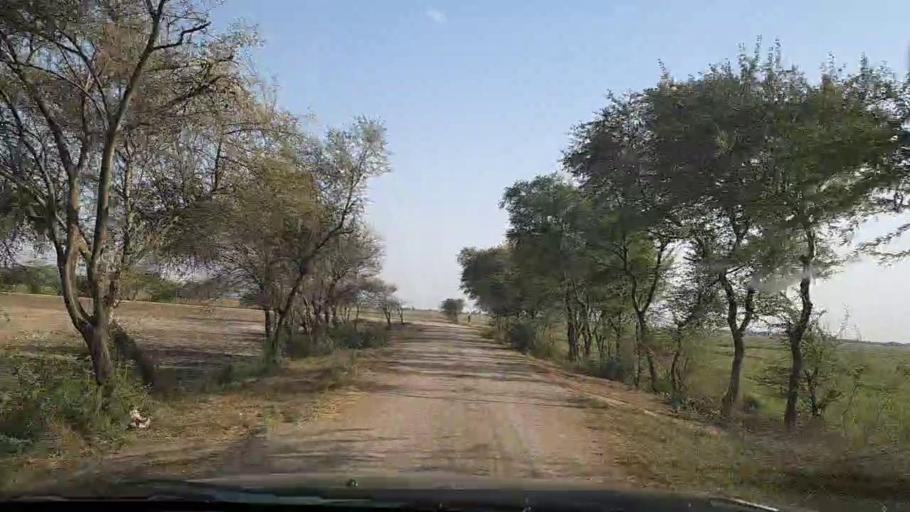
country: PK
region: Sindh
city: Chuhar Jamali
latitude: 24.5485
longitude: 68.1066
